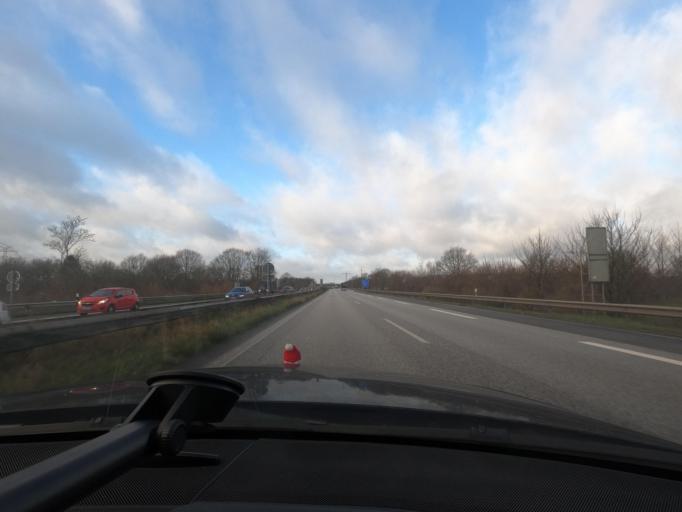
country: DE
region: Schleswig-Holstein
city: Borgstedt
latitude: 54.3429
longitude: 9.7078
